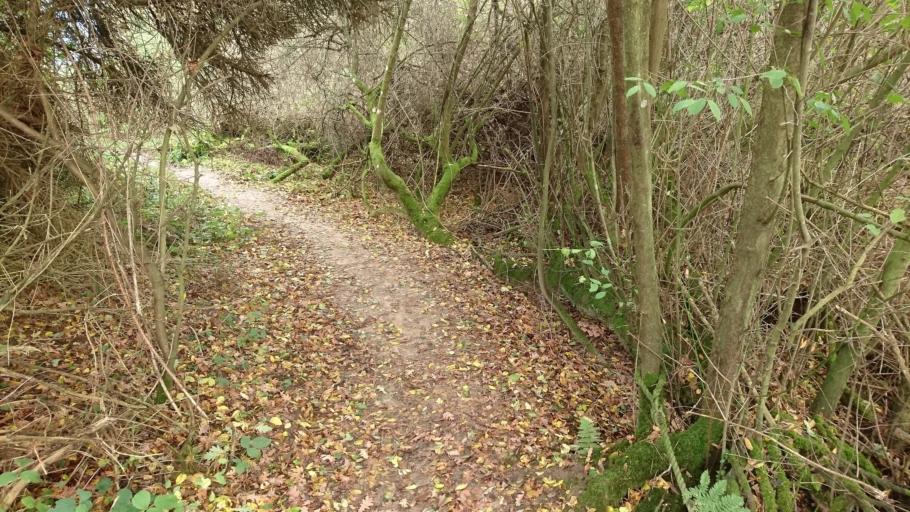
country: DK
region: North Denmark
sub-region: Morso Kommune
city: Nykobing Mors
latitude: 56.8379
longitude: 8.9645
